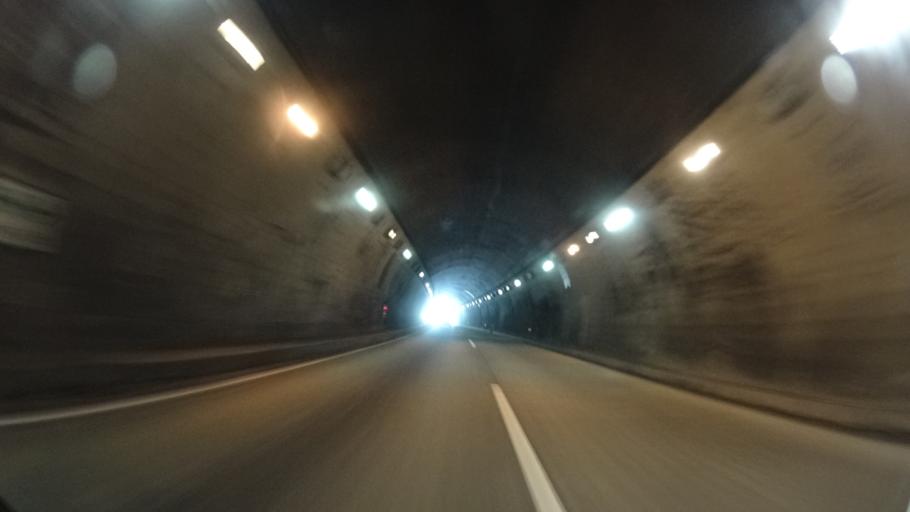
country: JP
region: Kumamoto
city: Hitoyoshi
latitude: 32.3362
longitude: 130.7356
